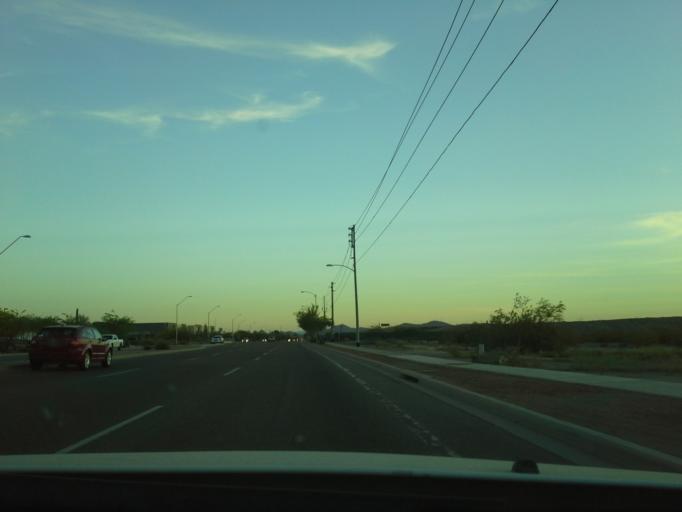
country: US
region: Arizona
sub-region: Maricopa County
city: Glendale
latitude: 33.6832
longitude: -112.0658
